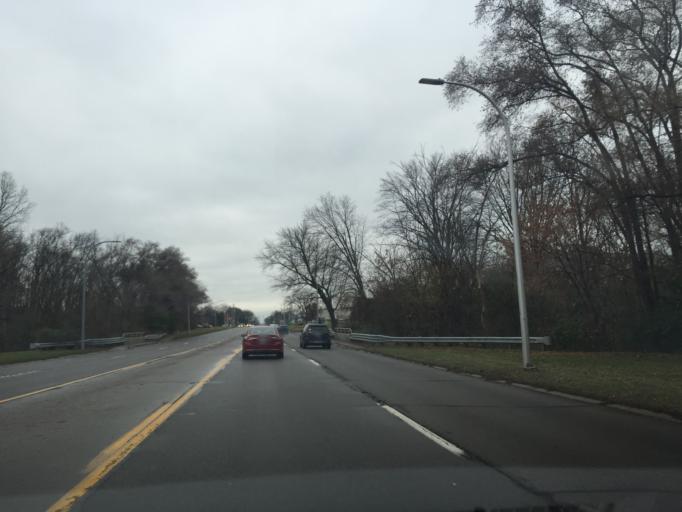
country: US
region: Michigan
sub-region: Wayne County
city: Redford
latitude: 42.4162
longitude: -83.3354
